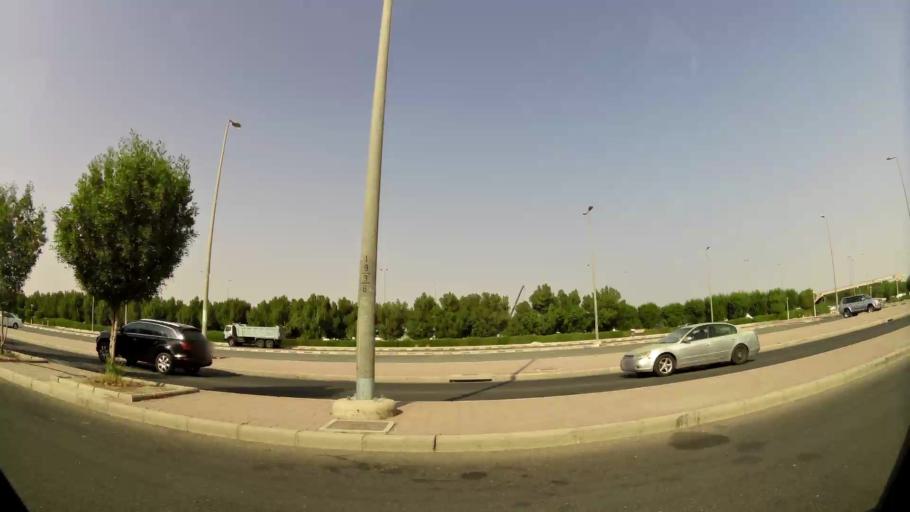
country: KW
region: Muhafazat al Jahra'
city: Al Jahra'
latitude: 29.3468
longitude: 47.6977
